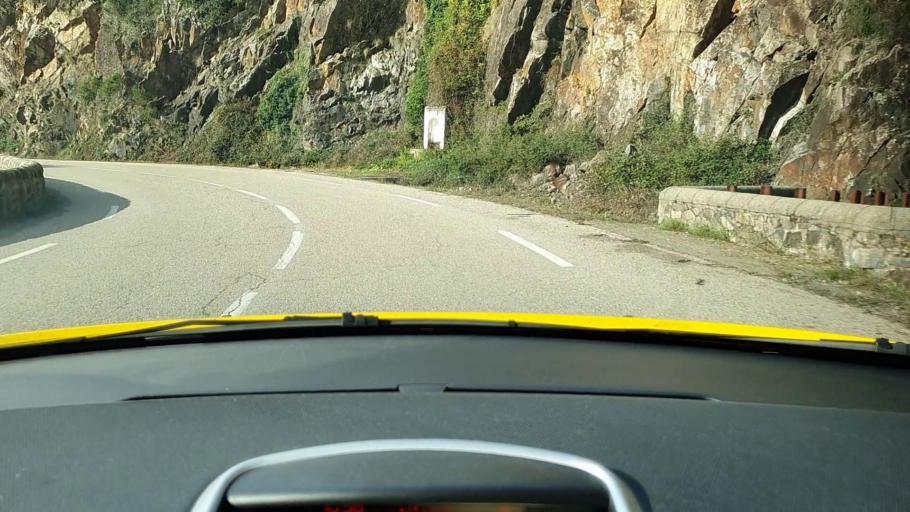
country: FR
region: Languedoc-Roussillon
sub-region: Departement du Gard
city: Lasalle
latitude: 44.1064
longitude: 3.8089
